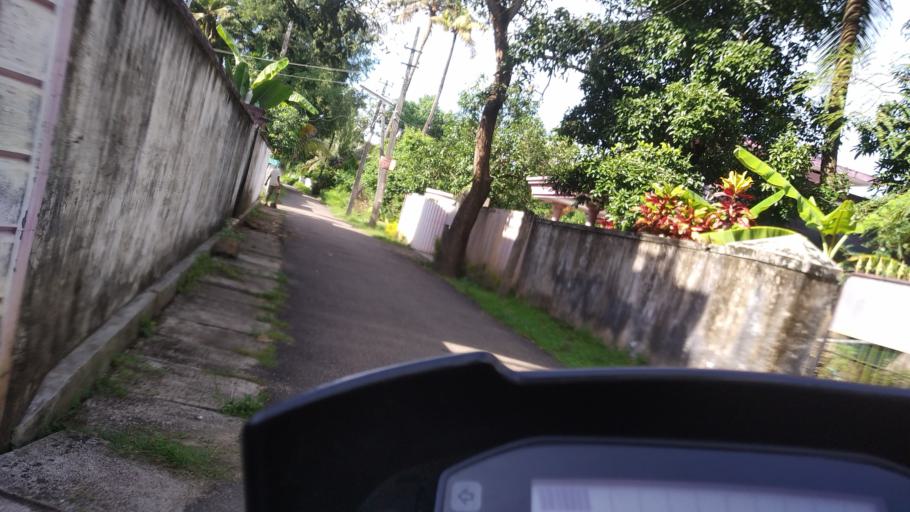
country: IN
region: Kerala
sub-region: Ernakulam
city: Elur
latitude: 10.0742
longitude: 76.2159
